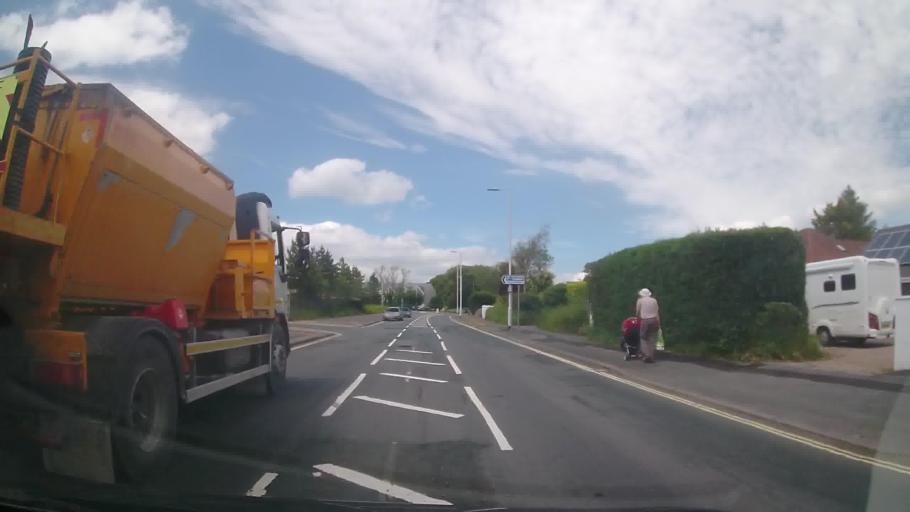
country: GB
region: England
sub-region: Devon
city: Plympton
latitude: 50.4271
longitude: -4.1095
